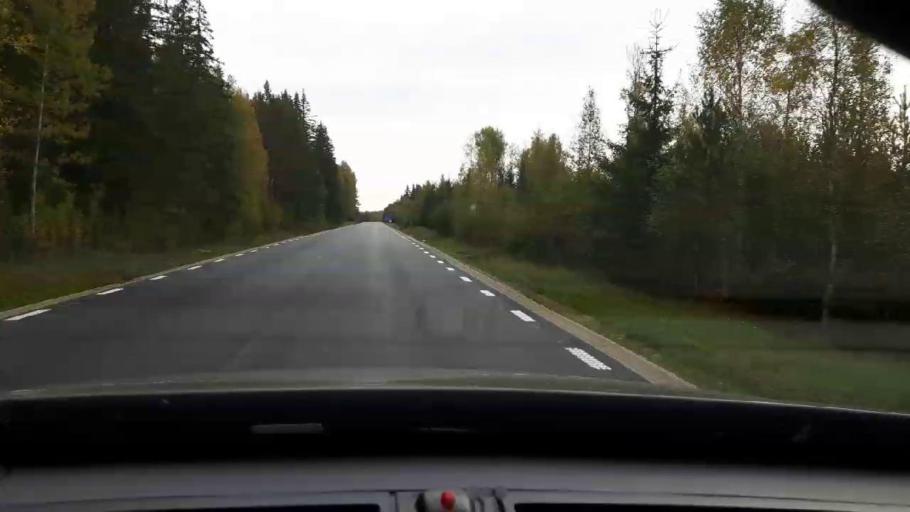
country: SE
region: Dalarna
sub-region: Ludvika Kommun
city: Grangesberg
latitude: 60.2415
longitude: 14.9832
